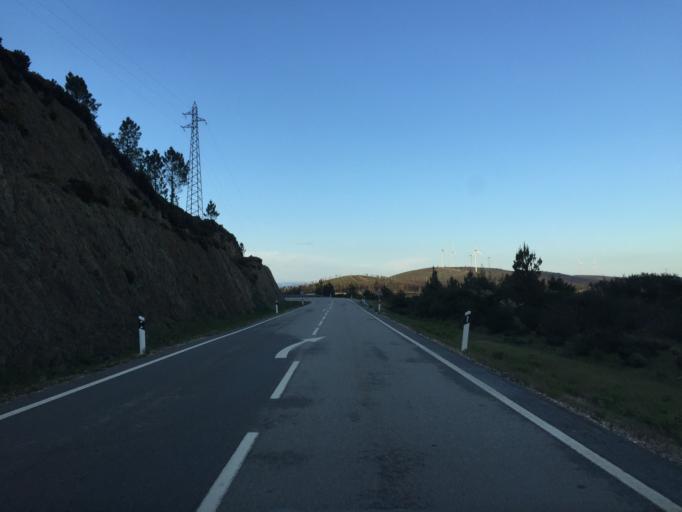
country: PT
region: Coimbra
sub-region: Gois
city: Gois
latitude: 40.1056
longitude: -8.0380
